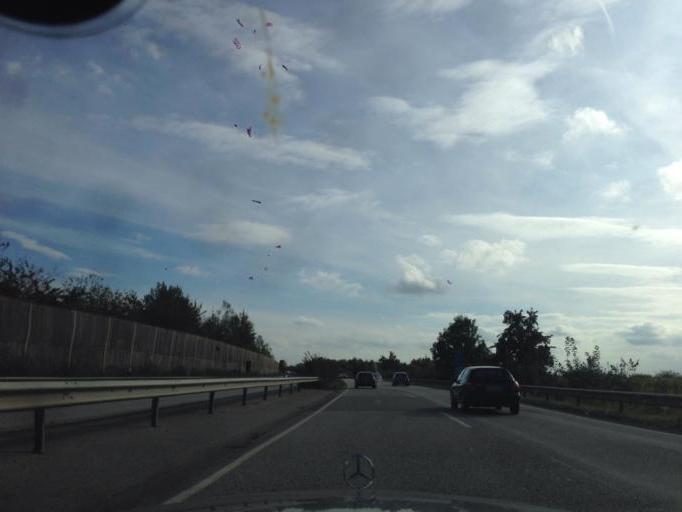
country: DE
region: Schleswig-Holstein
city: Hogersdorf
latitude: 53.9228
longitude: 10.2740
